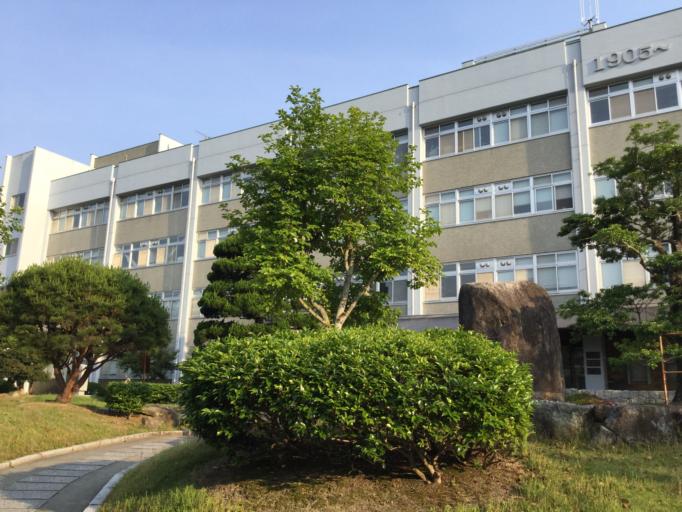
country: JP
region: Yamaguchi
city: Yamaguchi-shi
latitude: 34.1470
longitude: 131.4678
